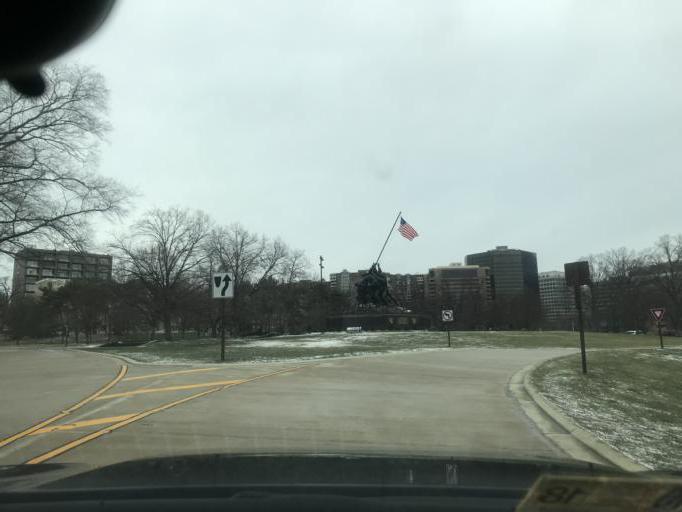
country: US
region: Washington, D.C.
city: Washington, D.C.
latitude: 38.8899
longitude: -77.0689
